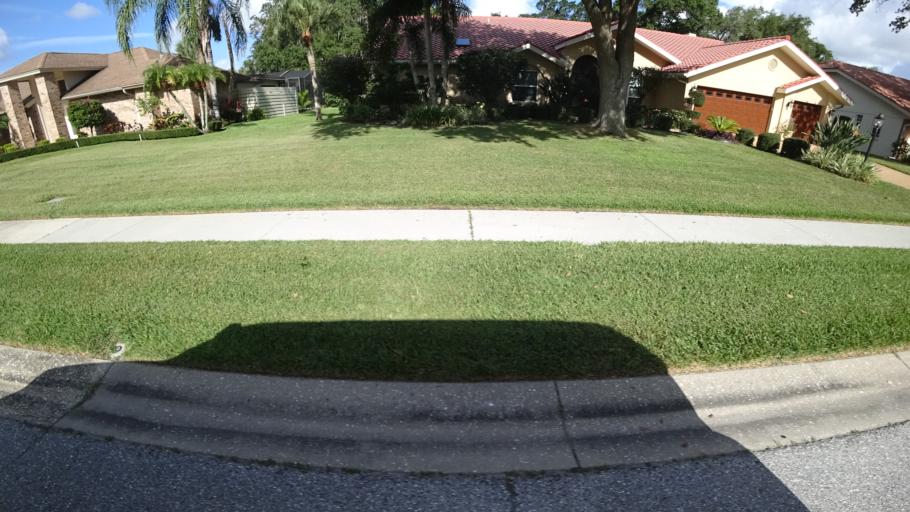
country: US
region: Florida
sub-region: Sarasota County
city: Desoto Lakes
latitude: 27.4007
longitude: -82.4855
